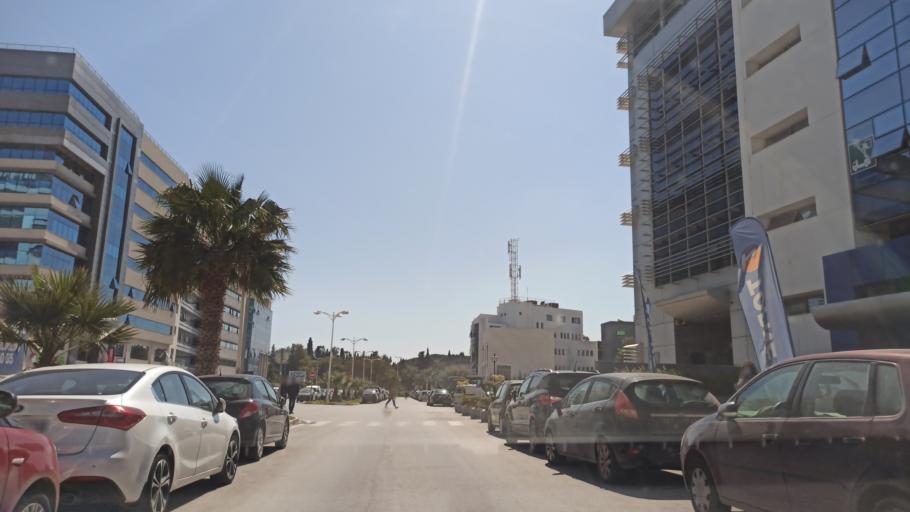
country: TN
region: Ariana
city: Ariana
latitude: 36.8489
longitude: 10.1962
